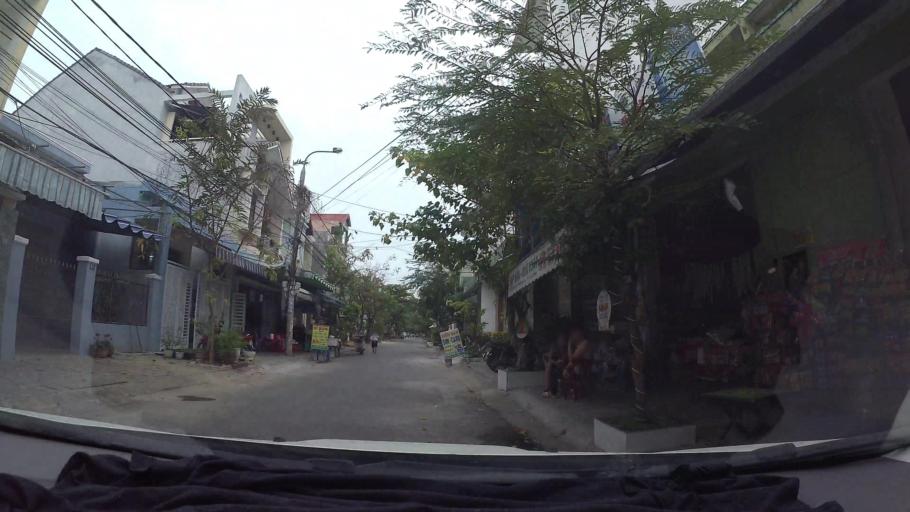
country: VN
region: Da Nang
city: Thanh Khe
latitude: 16.0608
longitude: 108.1814
